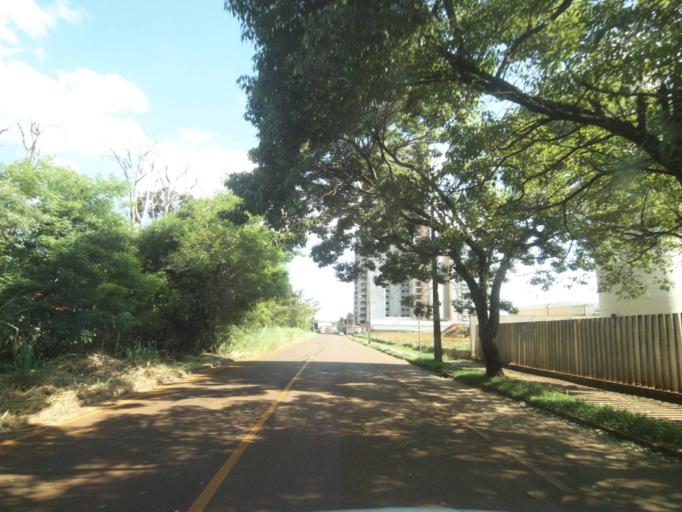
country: BR
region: Parana
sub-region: Londrina
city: Londrina
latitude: -23.3357
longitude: -51.1860
